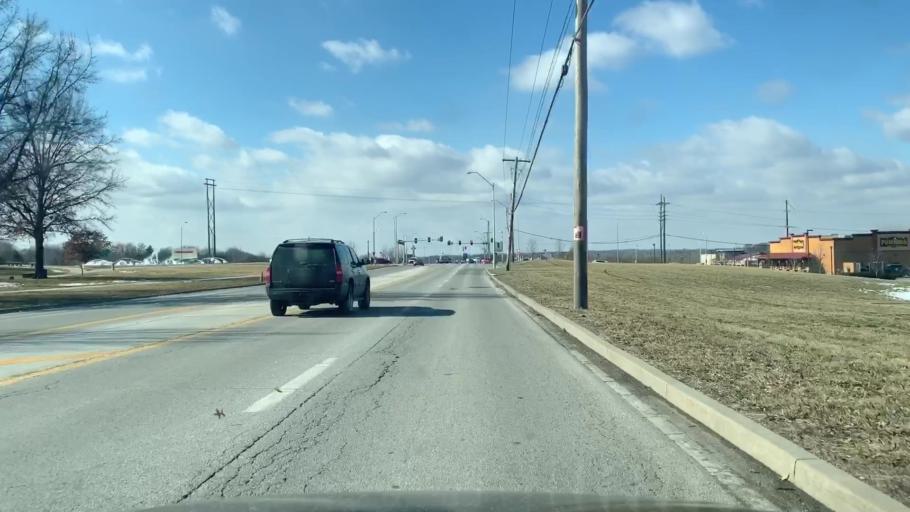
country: US
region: Missouri
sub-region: Clay County
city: Gladstone
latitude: 39.1813
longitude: -94.5743
